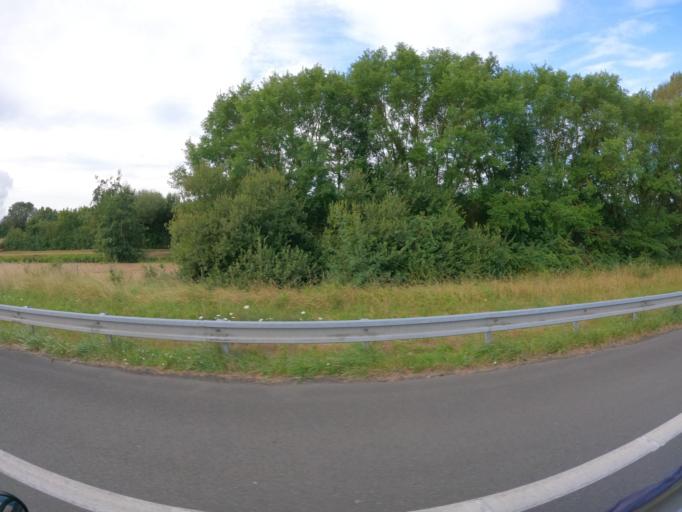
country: FR
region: Centre
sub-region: Departement d'Indre-et-Loire
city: Saint-Nicolas-de-Bourgueil
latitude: 47.2626
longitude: 0.1290
